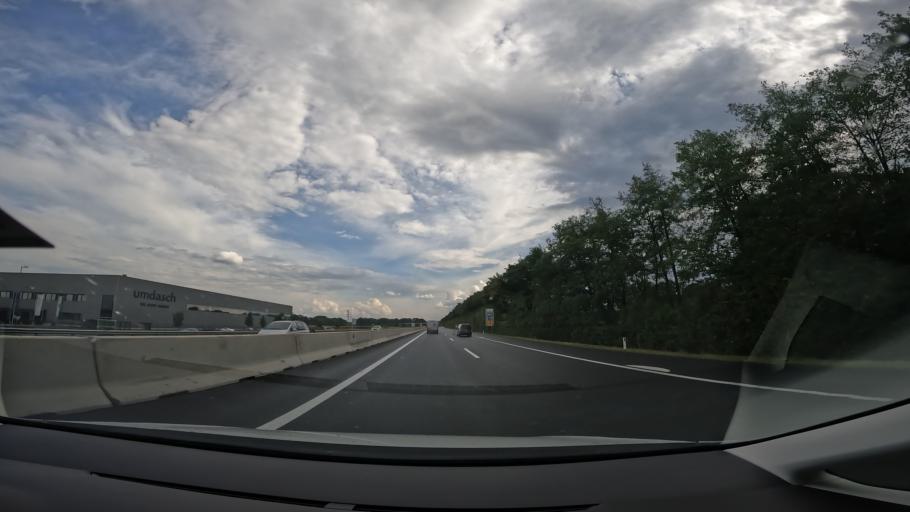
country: AT
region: Styria
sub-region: Politischer Bezirk Leibnitz
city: Gabersdorf
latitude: 46.8009
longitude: 15.5704
